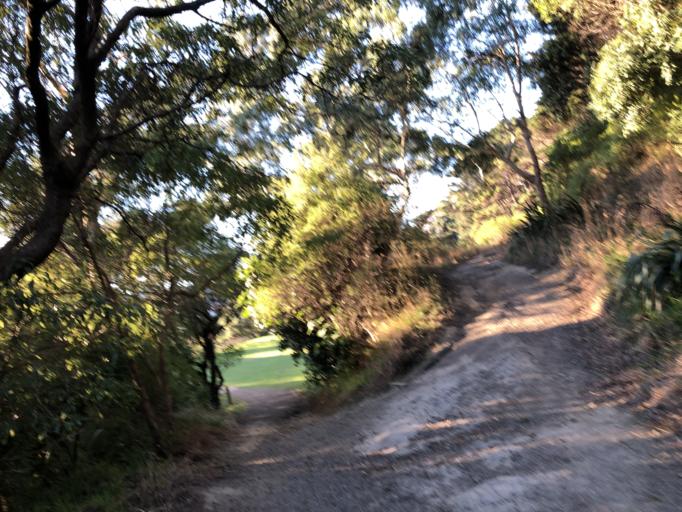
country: NZ
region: Wellington
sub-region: Wellington City
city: Wellington
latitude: -41.2973
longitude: 174.7906
